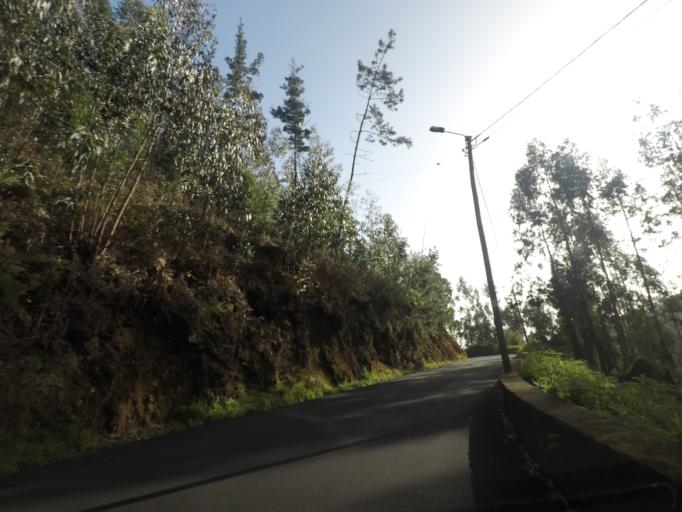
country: PT
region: Madeira
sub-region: Ribeira Brava
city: Campanario
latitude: 32.6719
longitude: -17.0035
